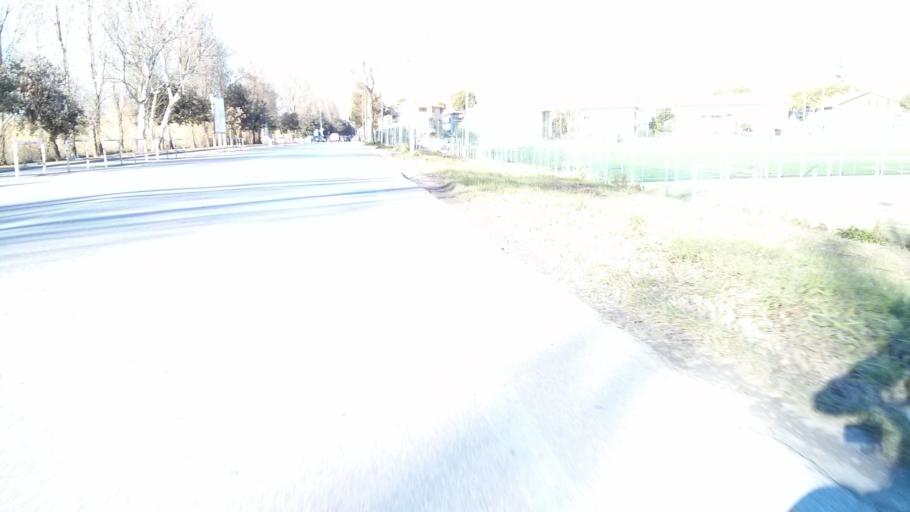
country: IT
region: The Marches
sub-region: Provincia di Pesaro e Urbino
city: Fano
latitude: 43.8301
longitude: 13.0148
